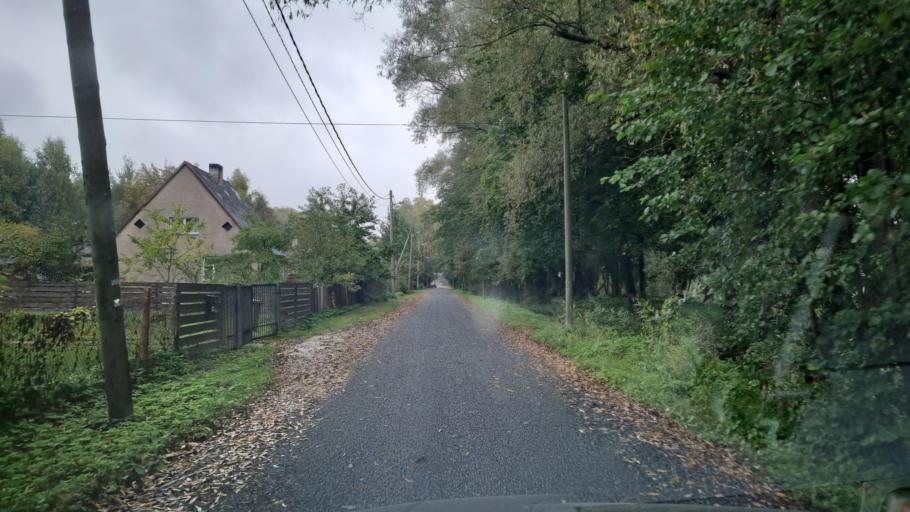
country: LV
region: Marupe
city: Marupe
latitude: 56.9384
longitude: 24.0144
